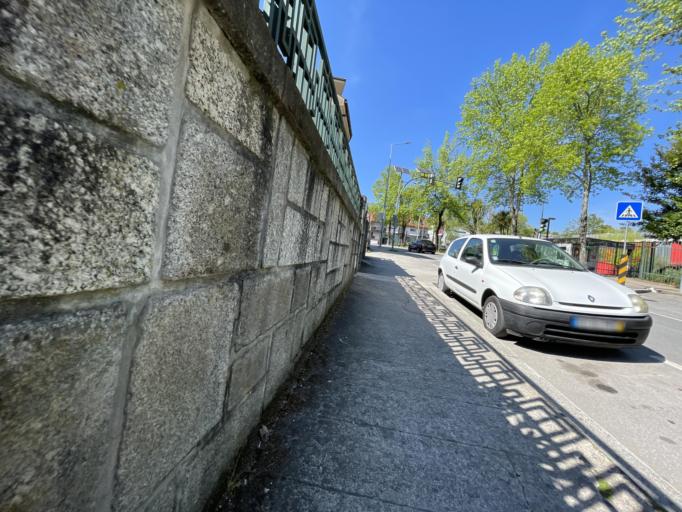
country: PT
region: Braga
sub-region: Guimaraes
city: Guimaraes
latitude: 41.4450
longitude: -8.2844
